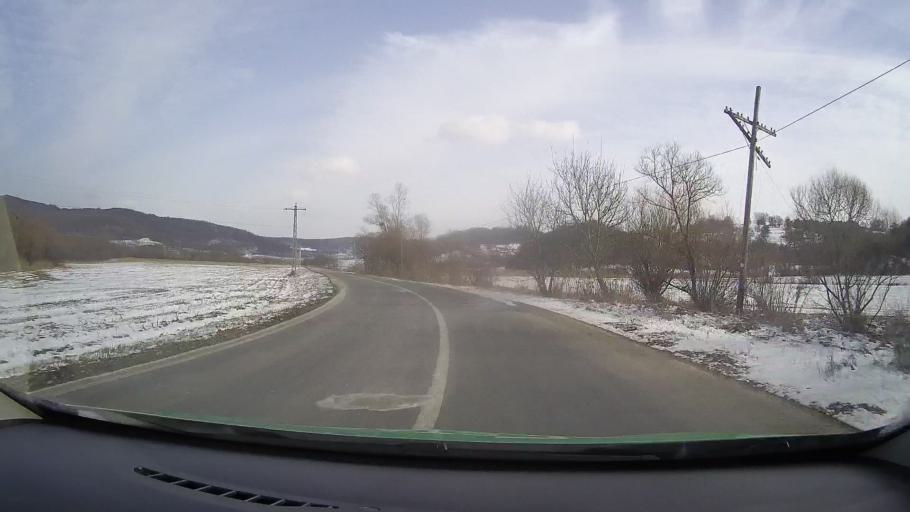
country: RO
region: Mures
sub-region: Comuna Apold
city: Apold
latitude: 46.1417
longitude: 24.7997
